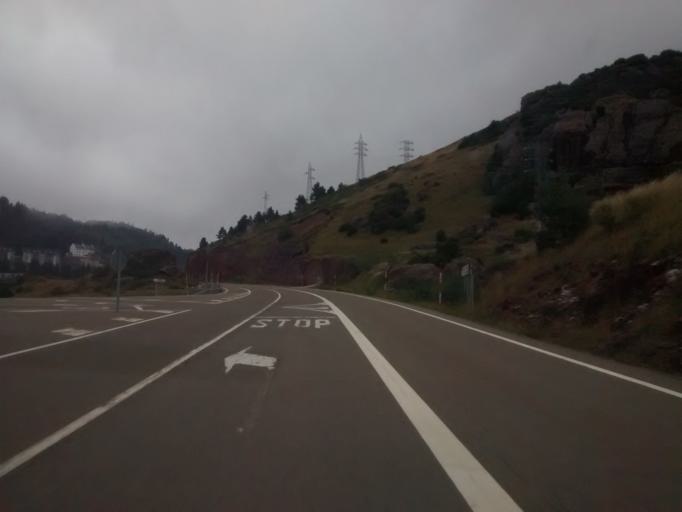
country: ES
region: Aragon
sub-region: Provincia de Huesca
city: Canfranc
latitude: 42.7842
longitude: -0.5220
